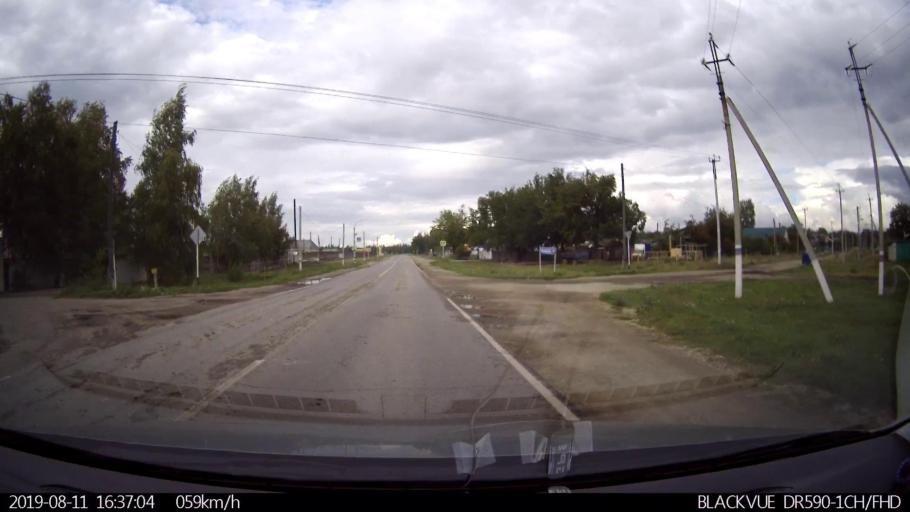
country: RU
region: Ulyanovsk
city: Mayna
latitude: 54.1243
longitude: 47.6120
